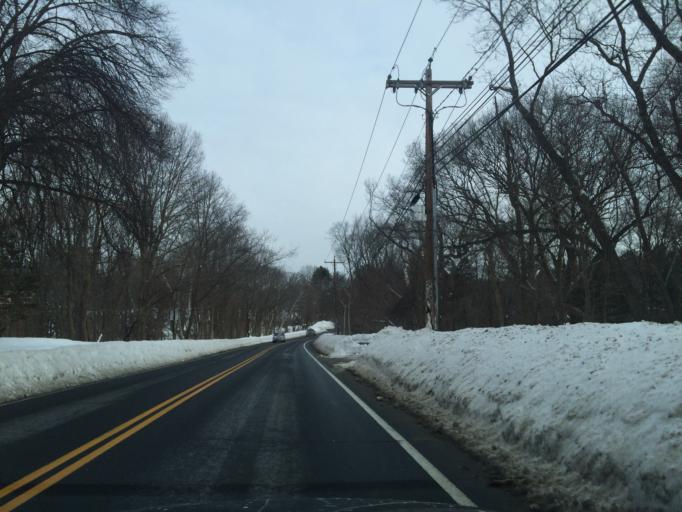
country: US
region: Massachusetts
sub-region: Middlesex County
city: Weston
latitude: 42.3500
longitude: -71.3060
